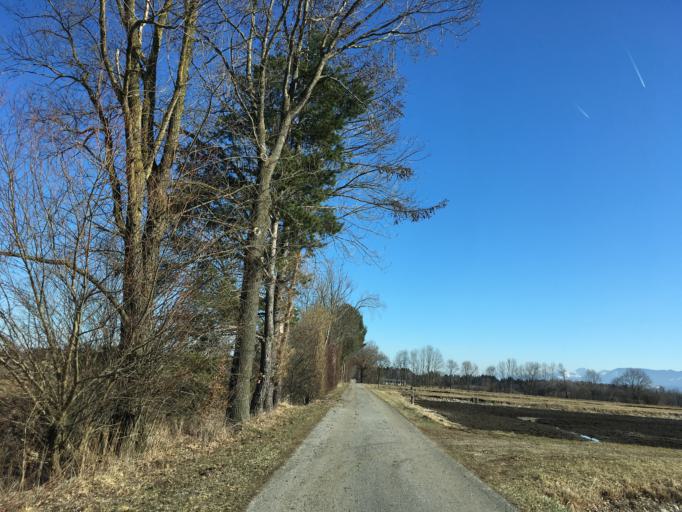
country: DE
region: Bavaria
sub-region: Upper Bavaria
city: Bad Aibling
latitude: 47.8308
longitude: 11.9997
